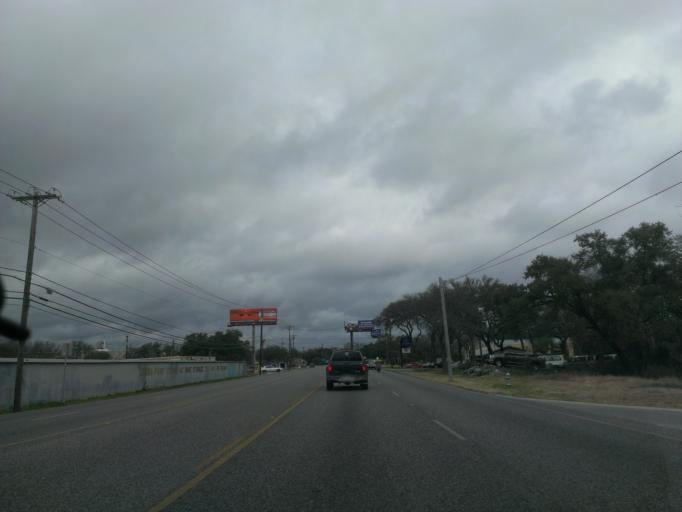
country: US
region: Texas
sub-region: Williamson County
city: Anderson Mill
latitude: 30.4011
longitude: -97.8517
